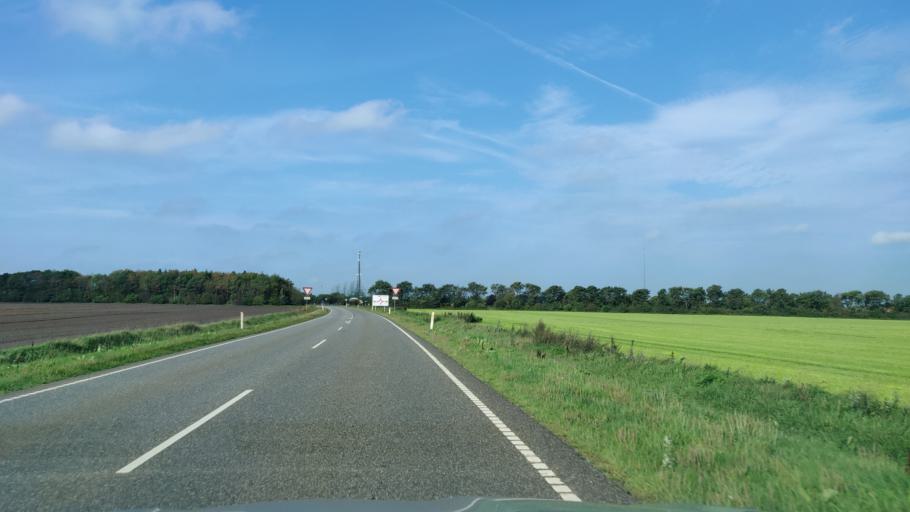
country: DK
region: Central Jutland
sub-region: Herning Kommune
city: Sunds
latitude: 56.2661
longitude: 9.0097
